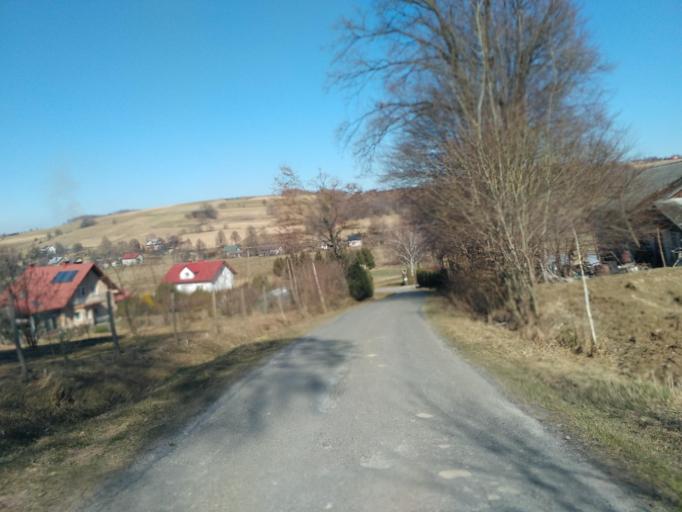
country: PL
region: Subcarpathian Voivodeship
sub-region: Powiat ropczycko-sedziszowski
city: Wielopole Skrzynskie
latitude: 49.9534
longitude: 21.5840
